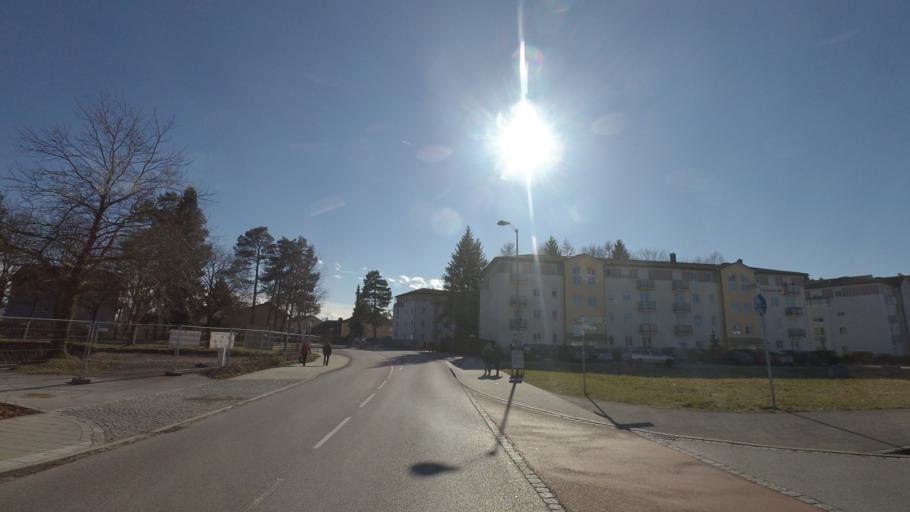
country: DE
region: Bavaria
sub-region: Upper Bavaria
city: Traunreut
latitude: 47.9635
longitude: 12.5862
